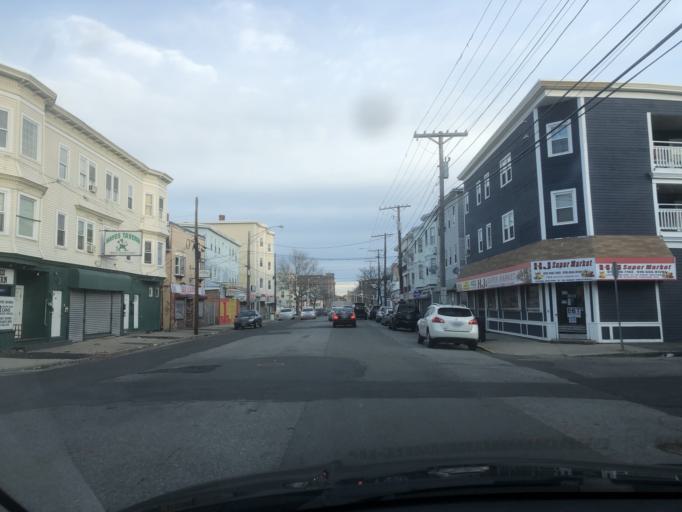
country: US
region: Massachusetts
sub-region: Essex County
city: Lawrence
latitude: 42.6975
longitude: -71.1534
